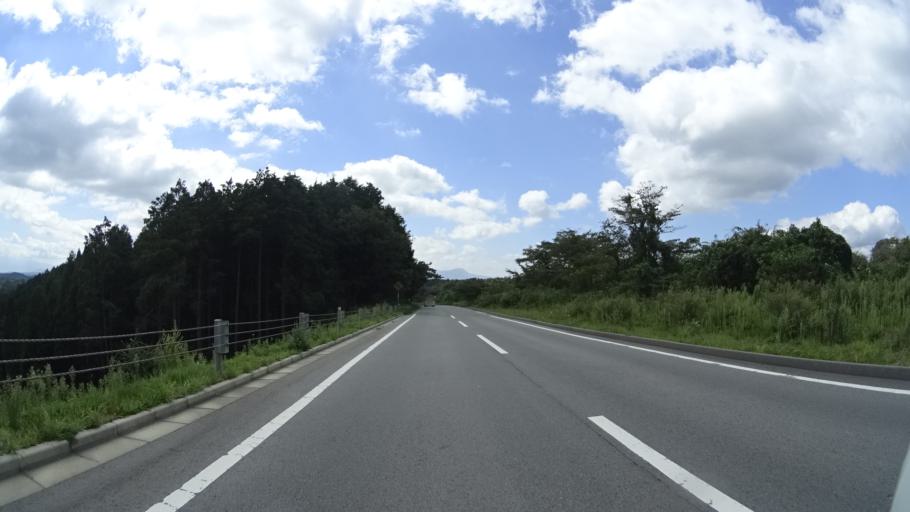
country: JP
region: Kumamoto
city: Aso
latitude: 33.0477
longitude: 131.1677
